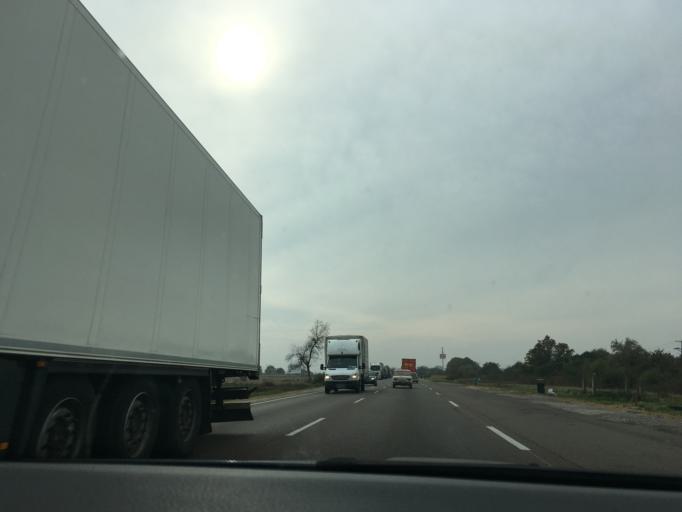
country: HU
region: Jasz-Nagykun-Szolnok
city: Kisujszallas
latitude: 47.2442
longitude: 20.8310
